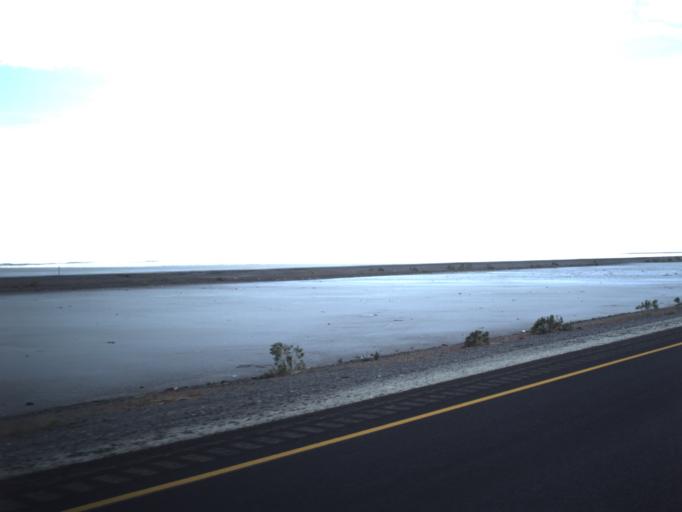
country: US
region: Utah
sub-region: Tooele County
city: Wendover
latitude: 40.7315
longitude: -113.5254
